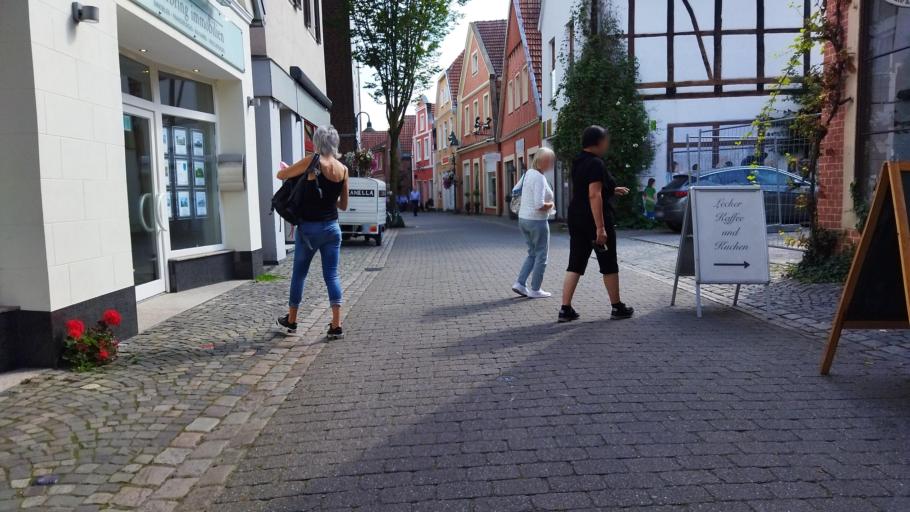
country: DE
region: North Rhine-Westphalia
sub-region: Regierungsbezirk Munster
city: Telgte
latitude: 51.9841
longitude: 7.7862
